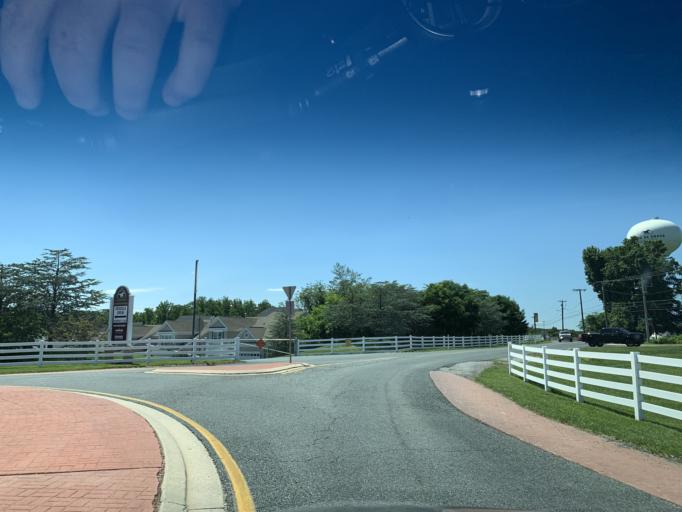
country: US
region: Maryland
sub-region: Harford County
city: Havre de Grace
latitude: 39.5548
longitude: -76.1281
